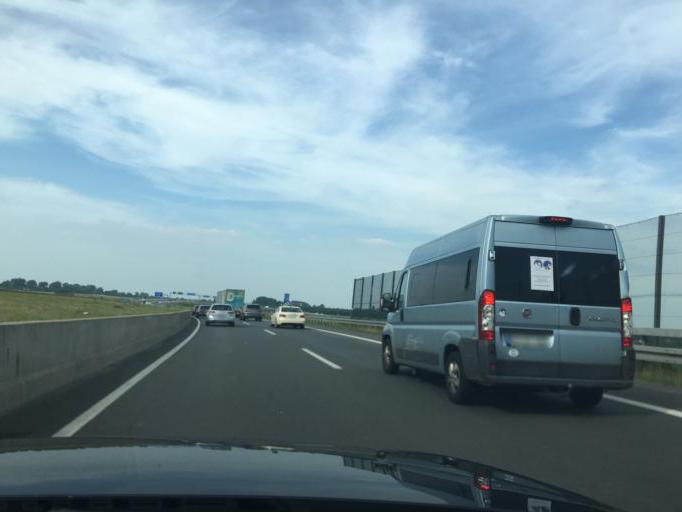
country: DE
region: North Rhine-Westphalia
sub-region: Regierungsbezirk Dusseldorf
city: Hochfeld
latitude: 51.3466
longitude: 6.7540
